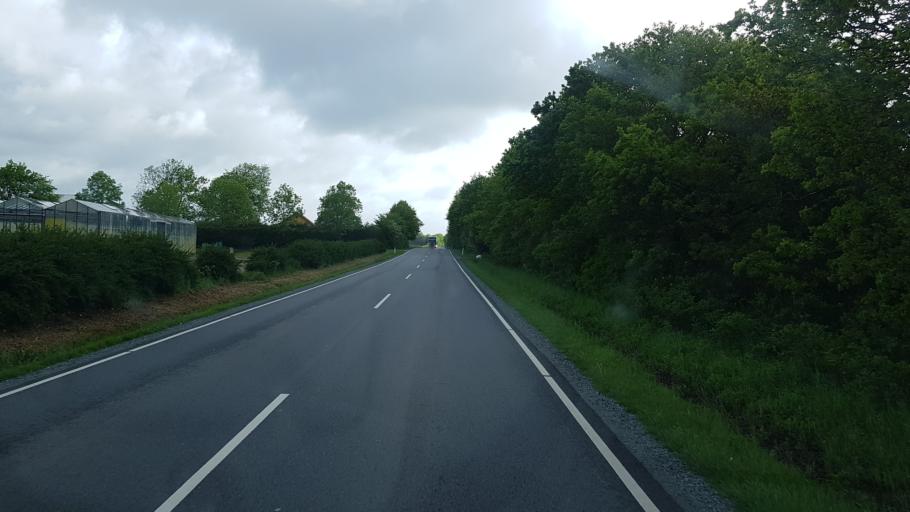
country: DK
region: South Denmark
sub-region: Vejen Kommune
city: Vejen
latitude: 55.4610
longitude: 9.1678
